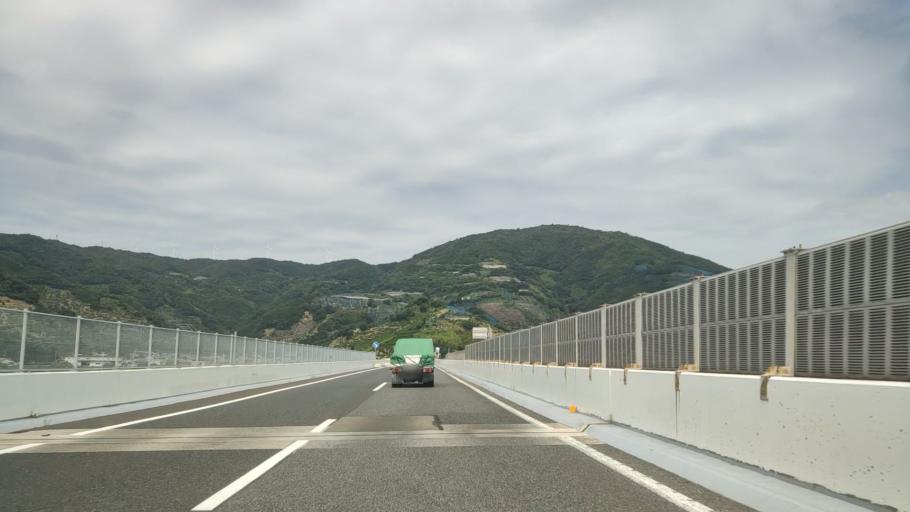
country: JP
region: Wakayama
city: Kainan
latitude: 34.0694
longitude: 135.2004
